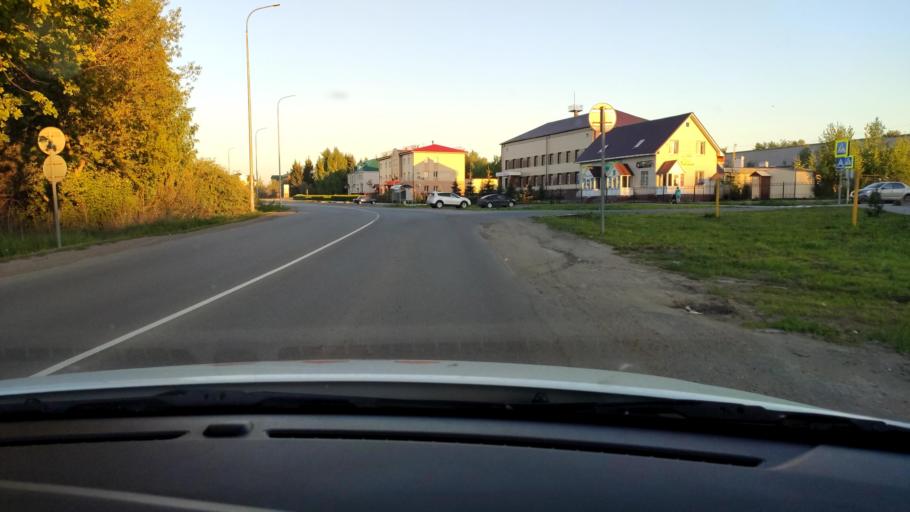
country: RU
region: Tatarstan
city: Vysokaya Gora
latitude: 55.9225
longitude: 49.3059
